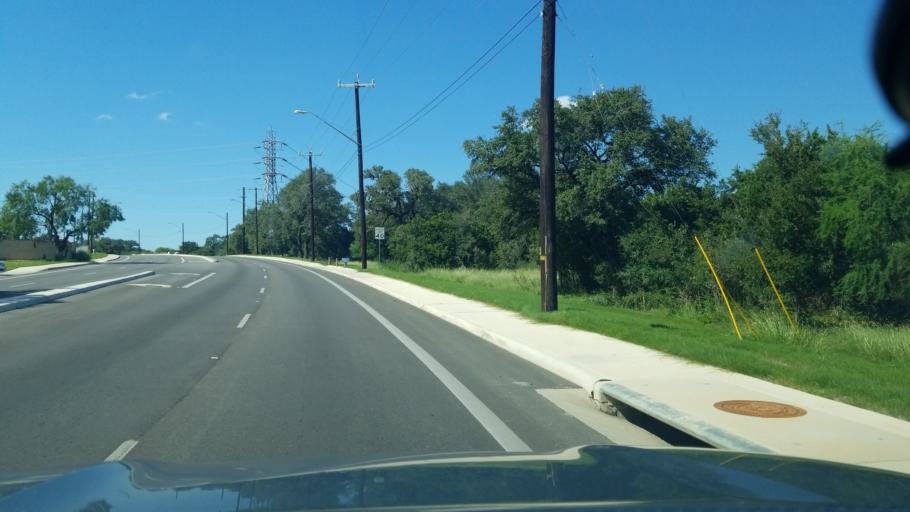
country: US
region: Texas
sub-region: Bexar County
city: Hollywood Park
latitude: 29.5957
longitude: -98.4356
